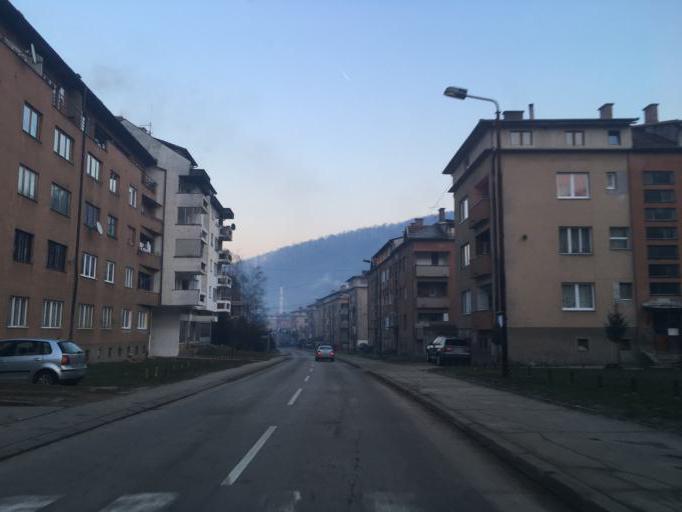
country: BA
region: Federation of Bosnia and Herzegovina
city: Novi Travnik
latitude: 44.1688
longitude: 17.6462
